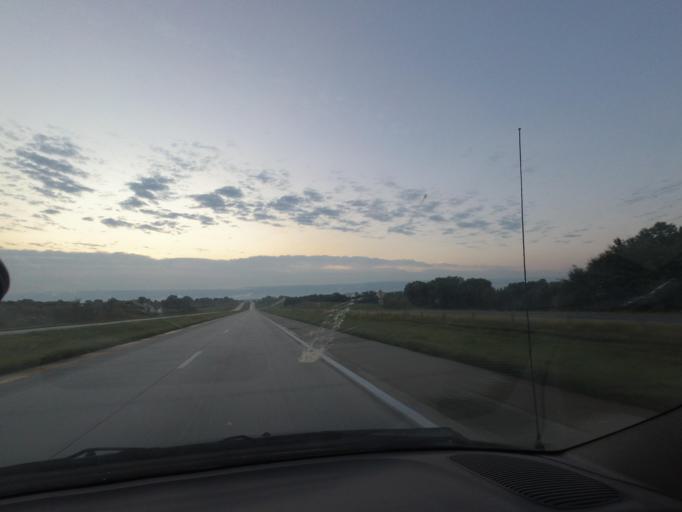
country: US
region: Missouri
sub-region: Macon County
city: Macon
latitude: 39.7571
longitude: -92.6362
